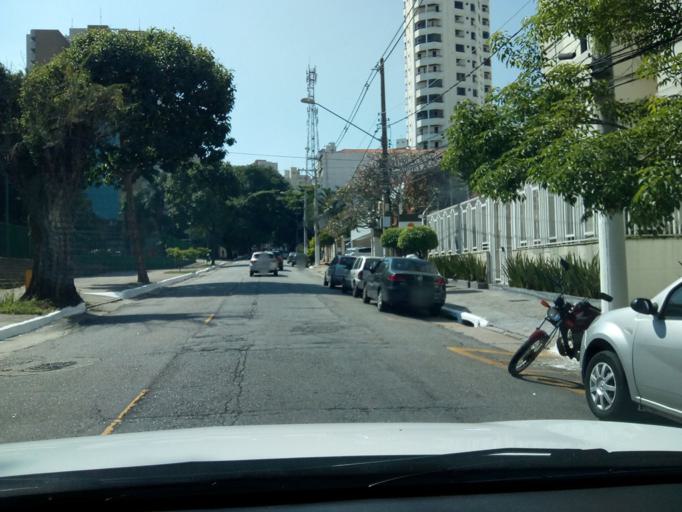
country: BR
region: Sao Paulo
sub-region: Sao Paulo
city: Sao Paulo
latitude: -23.5790
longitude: -46.6538
